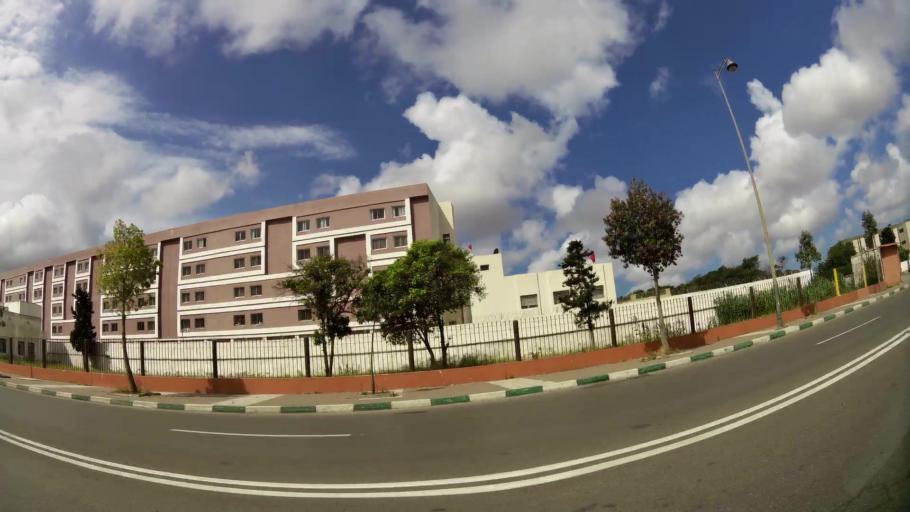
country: MA
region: Gharb-Chrarda-Beni Hssen
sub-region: Kenitra Province
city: Kenitra
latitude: 34.2569
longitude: -6.5622
